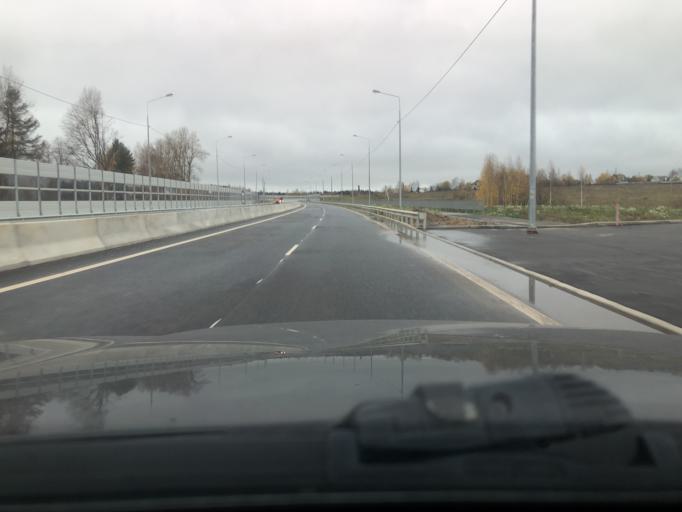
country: RU
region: Moskovskaya
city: Semkhoz
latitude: 56.3181
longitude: 38.0861
